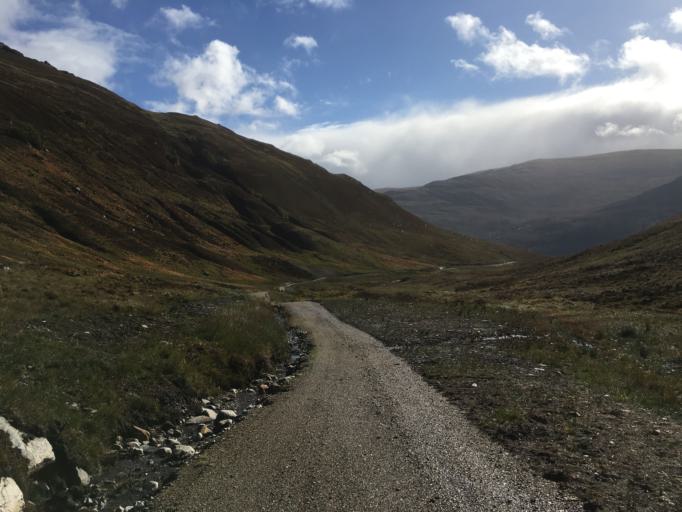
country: GB
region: Scotland
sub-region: Highland
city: Spean Bridge
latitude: 57.3524
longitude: -4.9884
